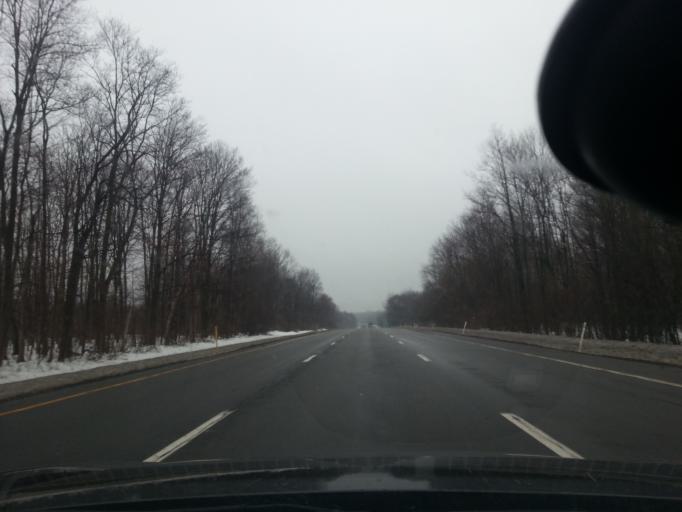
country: US
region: New York
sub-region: Jefferson County
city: Adams
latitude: 43.7351
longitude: -76.0752
